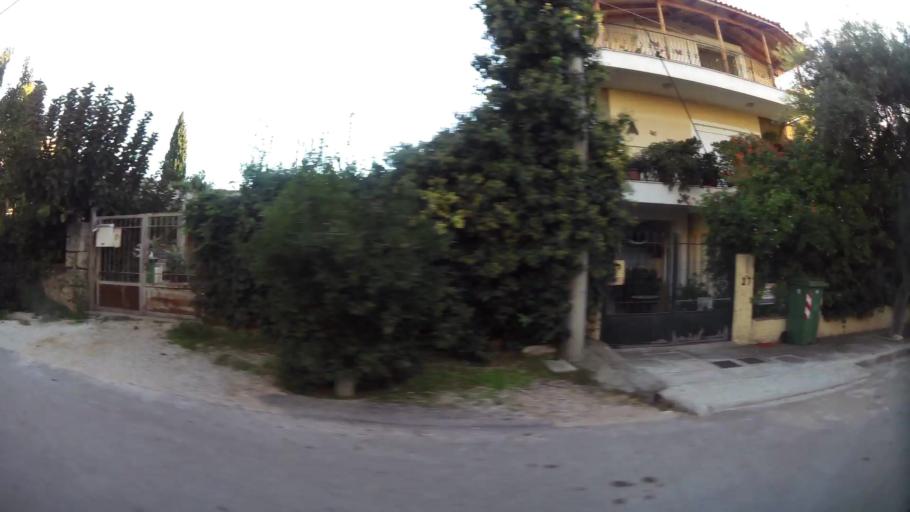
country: GR
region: Attica
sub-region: Nomarchia Athinas
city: Kifisia
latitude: 38.0731
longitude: 23.8012
